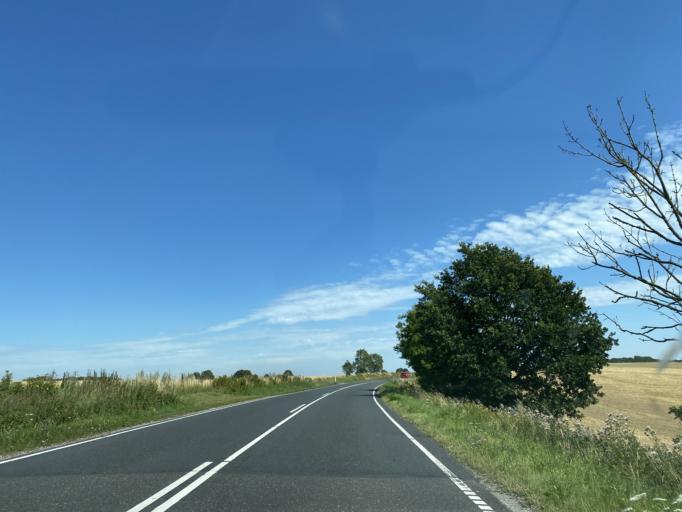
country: DK
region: South Denmark
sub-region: Kerteminde Kommune
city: Langeskov
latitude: 55.2511
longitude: 10.6195
